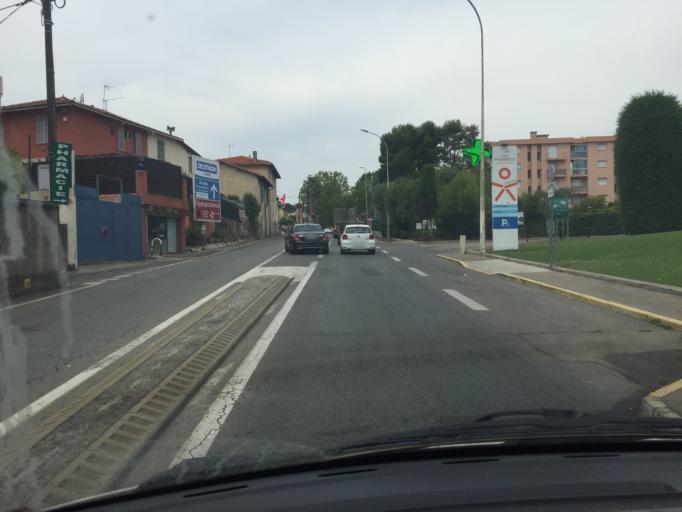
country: FR
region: Provence-Alpes-Cote d'Azur
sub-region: Departement des Alpes-Maritimes
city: Biot
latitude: 43.5943
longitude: 7.0942
